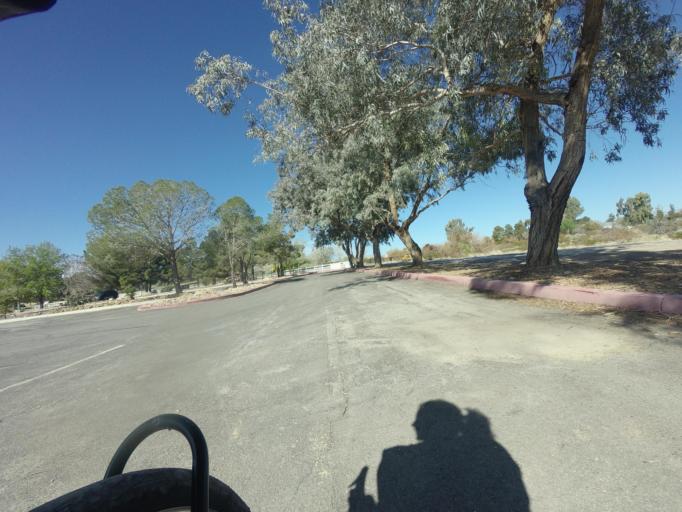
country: US
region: Nevada
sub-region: Clark County
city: North Las Vegas
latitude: 36.3249
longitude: -115.2623
